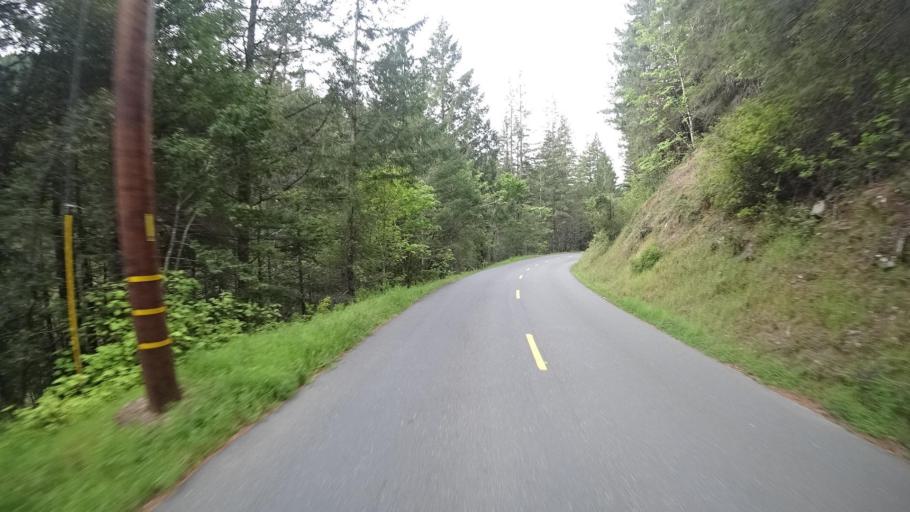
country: US
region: California
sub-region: Humboldt County
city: Redway
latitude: 40.2814
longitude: -123.8466
